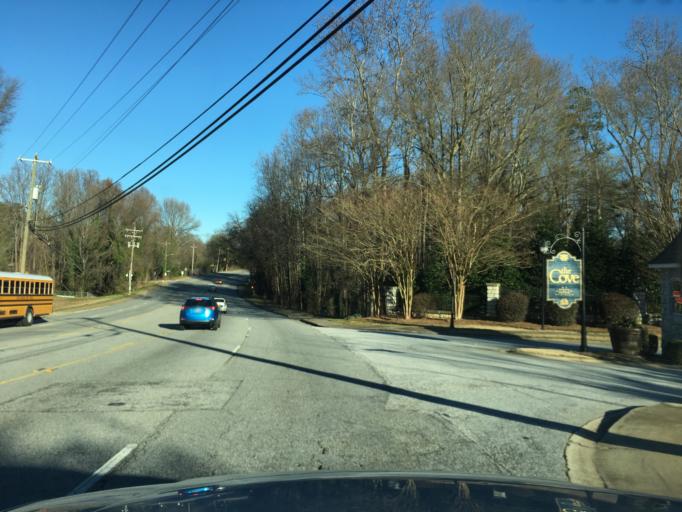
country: US
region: South Carolina
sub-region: Greenville County
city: Wade Hampton
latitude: 34.8714
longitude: -82.3395
